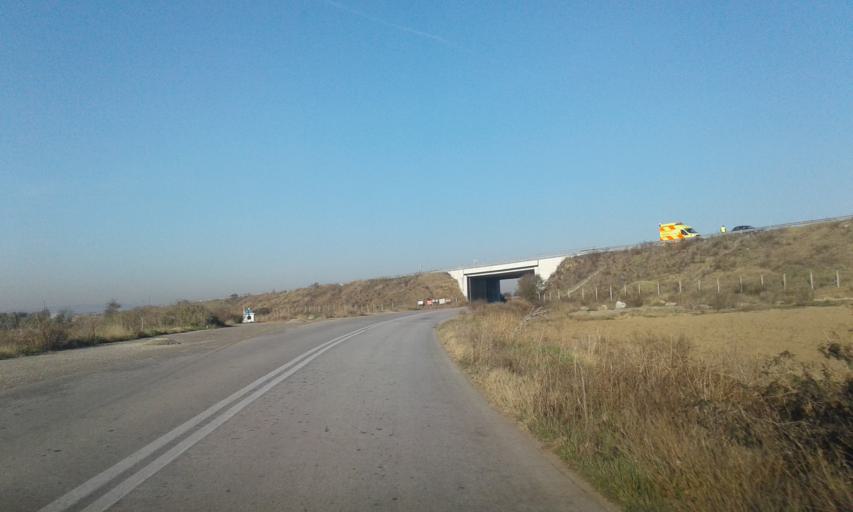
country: GR
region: Central Macedonia
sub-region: Nomos Thessalonikis
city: Kolchikon
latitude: 40.7087
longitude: 23.1830
